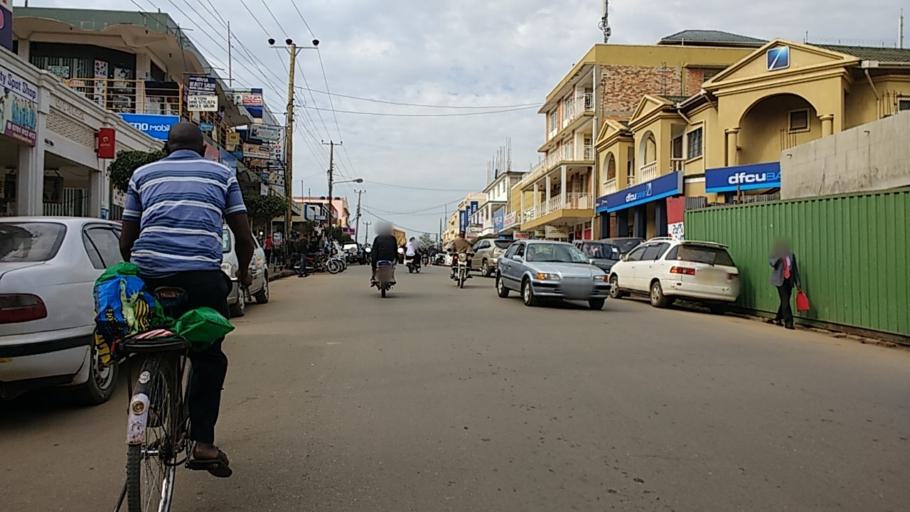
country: UG
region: Western Region
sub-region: Mbarara District
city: Mbarara
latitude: -0.6055
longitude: 30.6622
